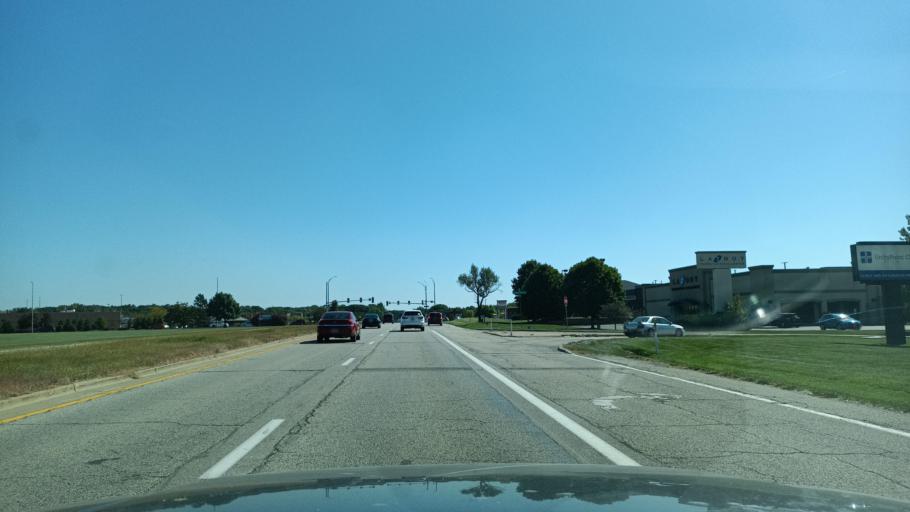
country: US
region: Illinois
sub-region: Peoria County
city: West Peoria
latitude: 40.7719
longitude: -89.6593
